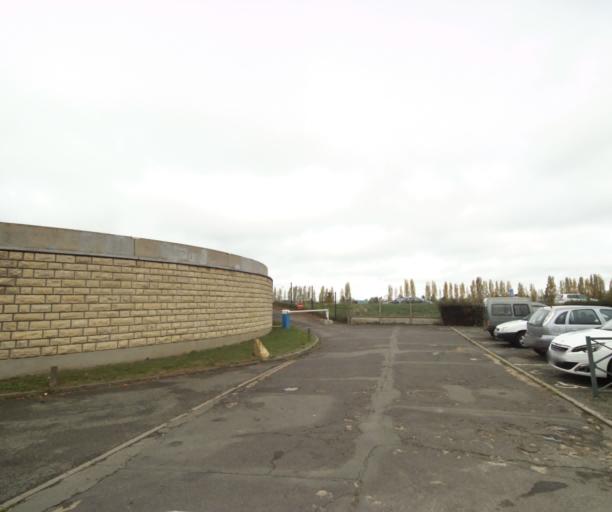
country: FR
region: Centre
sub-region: Departement d'Eure-et-Loir
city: Dreux
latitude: 48.7456
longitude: 1.3607
